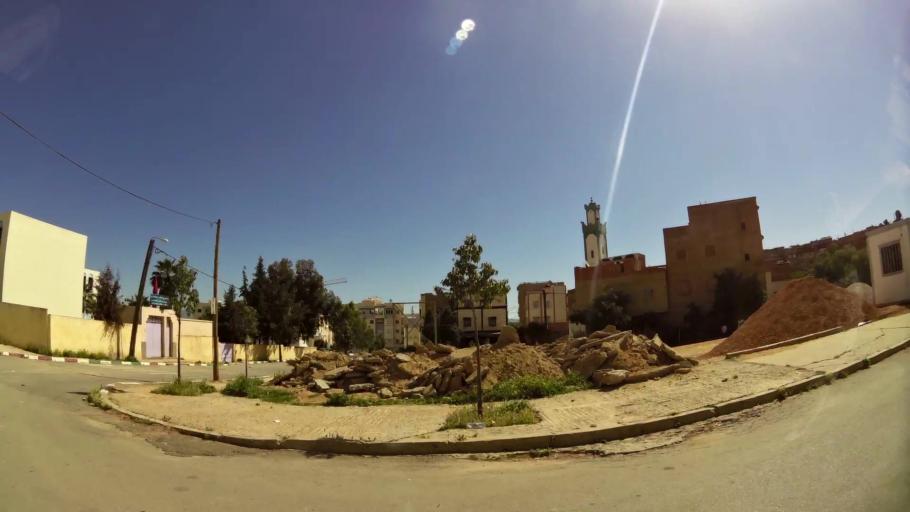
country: MA
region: Meknes-Tafilalet
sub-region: Meknes
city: Meknes
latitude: 33.9088
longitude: -5.5414
